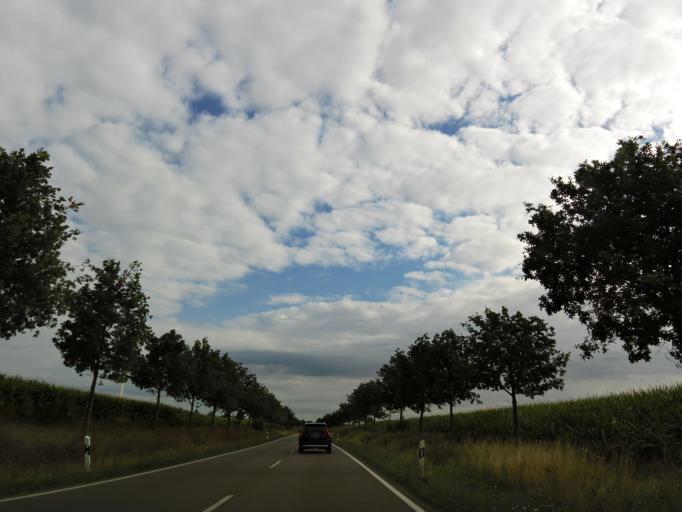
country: DE
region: Saxony
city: Markranstadt
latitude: 51.2810
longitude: 12.2819
